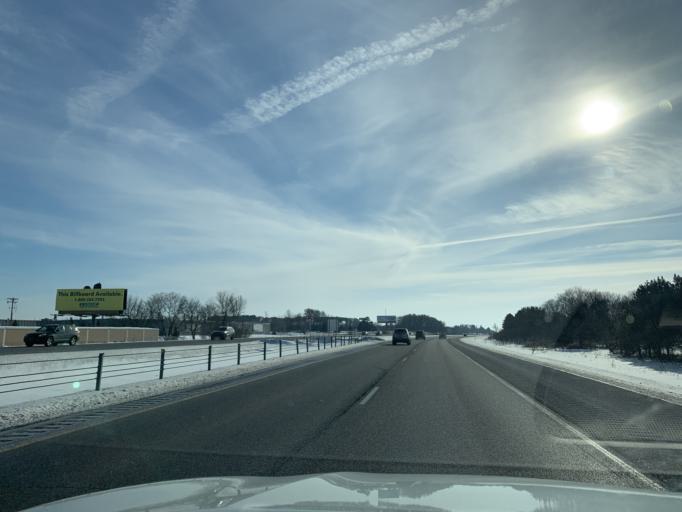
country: US
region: Minnesota
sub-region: Chisago County
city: Wyoming
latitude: 45.3266
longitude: -93.0040
